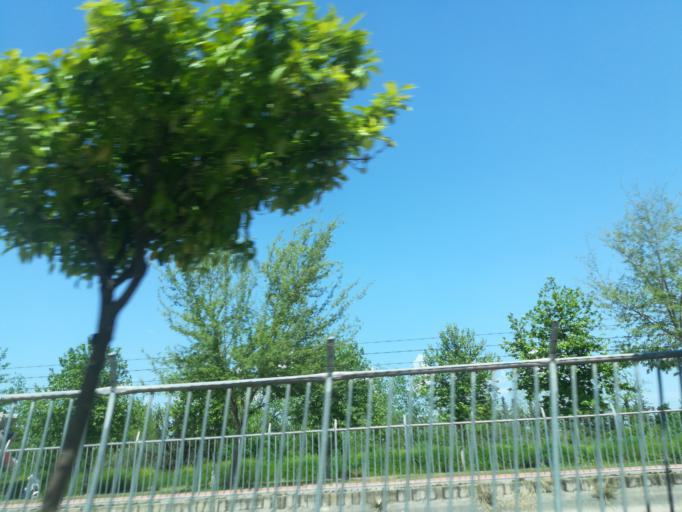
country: TR
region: Adana
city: Yuregir
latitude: 37.0198
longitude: 35.3728
